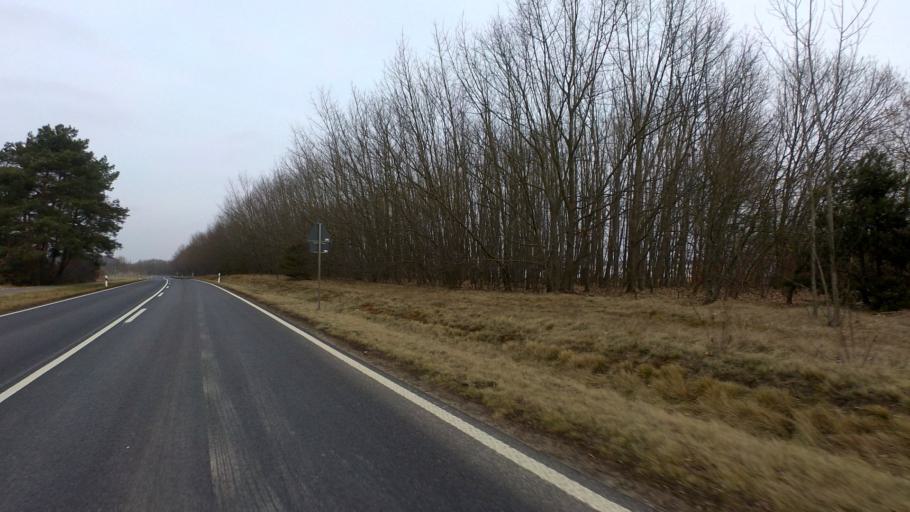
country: DE
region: Brandenburg
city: Beelitz
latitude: 52.2286
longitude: 13.0337
